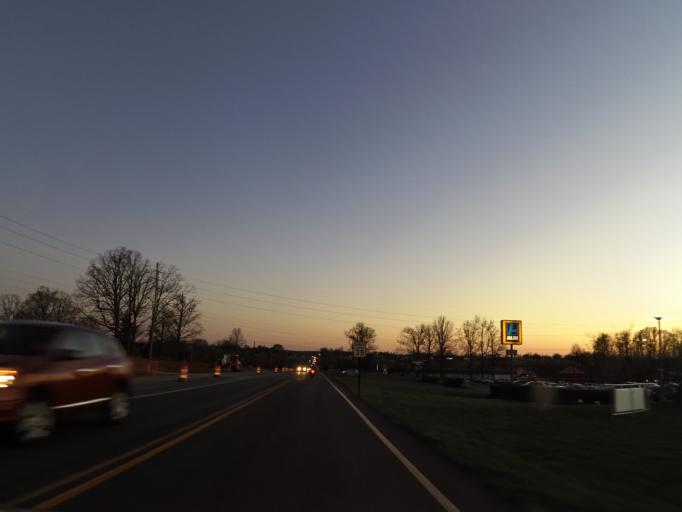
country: US
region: Tennessee
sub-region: Robertson County
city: Springfield
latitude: 36.4869
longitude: -86.8836
